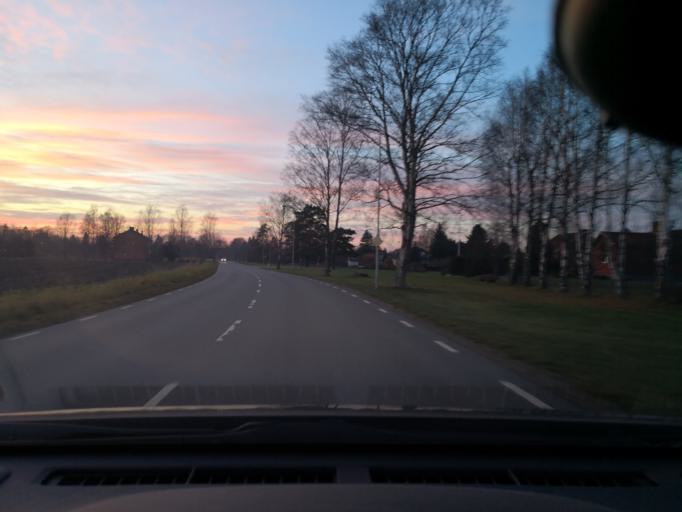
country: SE
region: OErebro
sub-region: Lindesbergs Kommun
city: Fellingsbro
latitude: 59.4301
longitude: 15.5895
